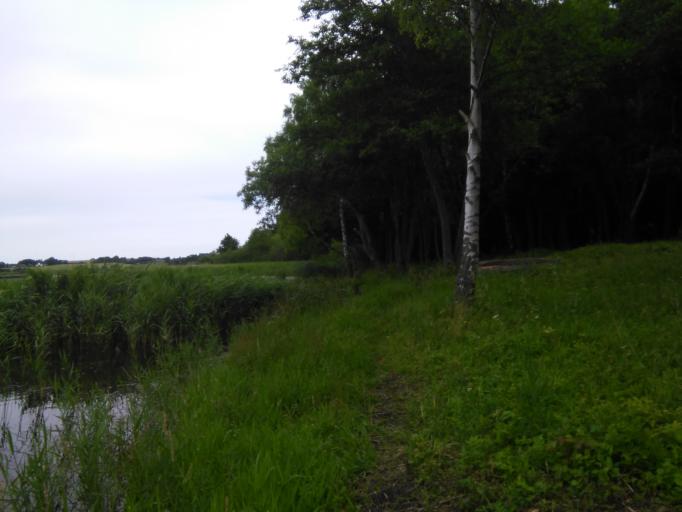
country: DK
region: Central Jutland
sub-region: Horsens Kommune
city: Horsens
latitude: 55.8712
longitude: 9.8915
